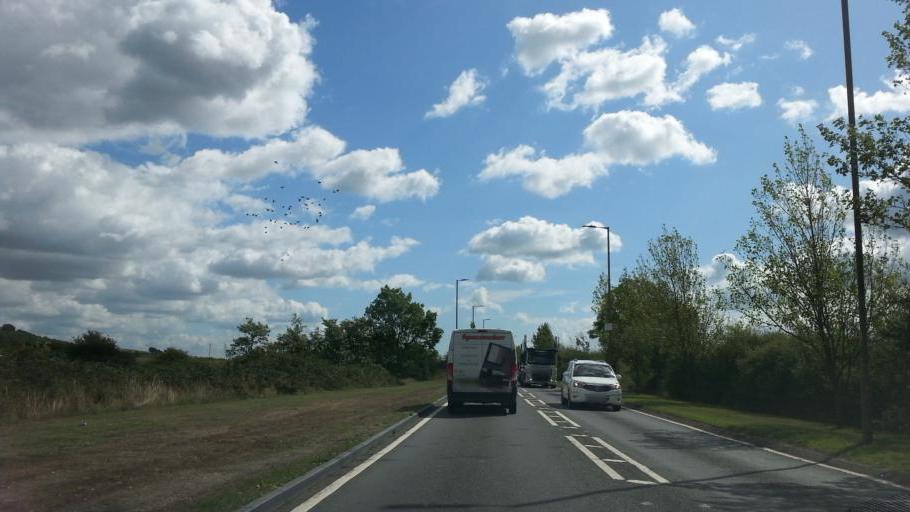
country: GB
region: England
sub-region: Essex
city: South Benfleet
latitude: 51.5402
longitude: 0.5556
